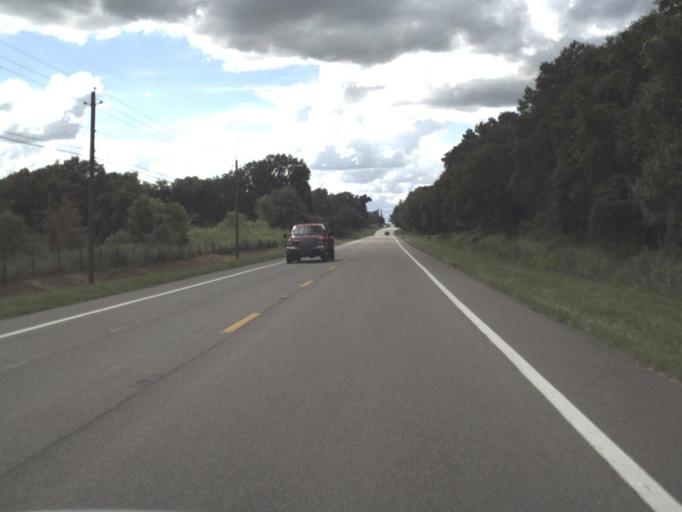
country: US
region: Florida
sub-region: Polk County
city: Highland City
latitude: 27.9968
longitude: -81.8806
